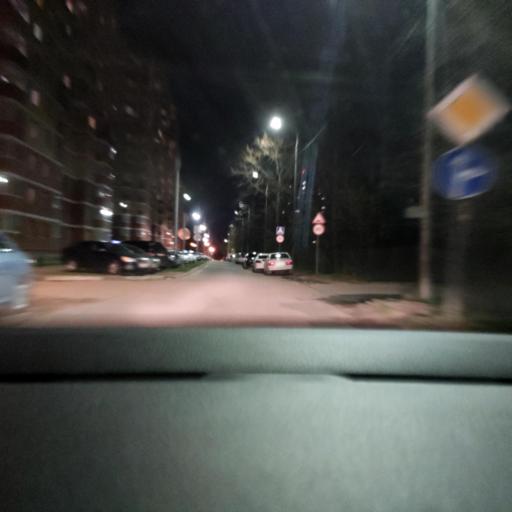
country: RU
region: Moskovskaya
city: Reutov
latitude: 55.7731
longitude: 37.8910
